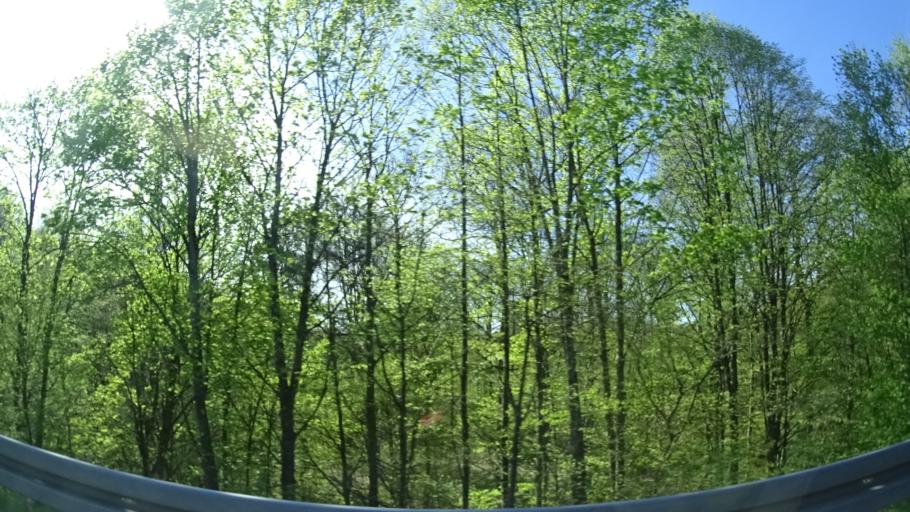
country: DE
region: Bavaria
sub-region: Regierungsbezirk Unterfranken
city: Burgpreppach
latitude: 50.0767
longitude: 10.6468
